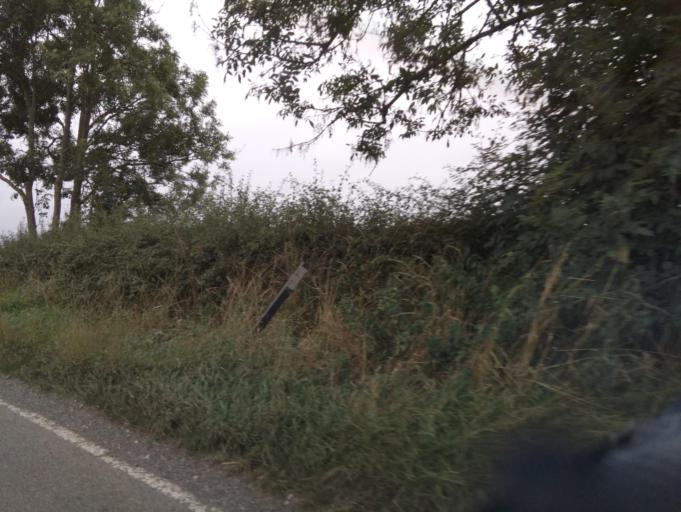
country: GB
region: England
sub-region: Derbyshire
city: Duffield
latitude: 53.0006
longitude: -1.5320
